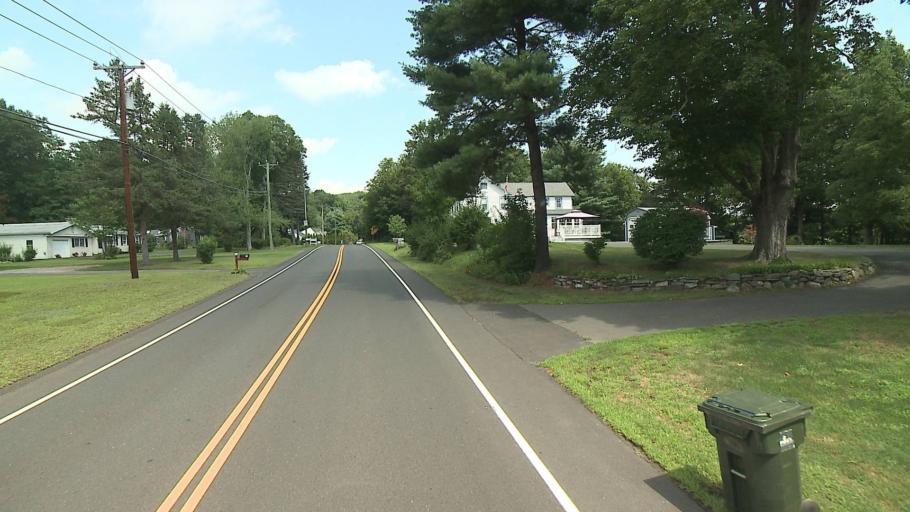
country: US
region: Connecticut
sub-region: Hartford County
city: Canton Valley
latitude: 41.8188
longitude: -72.8896
